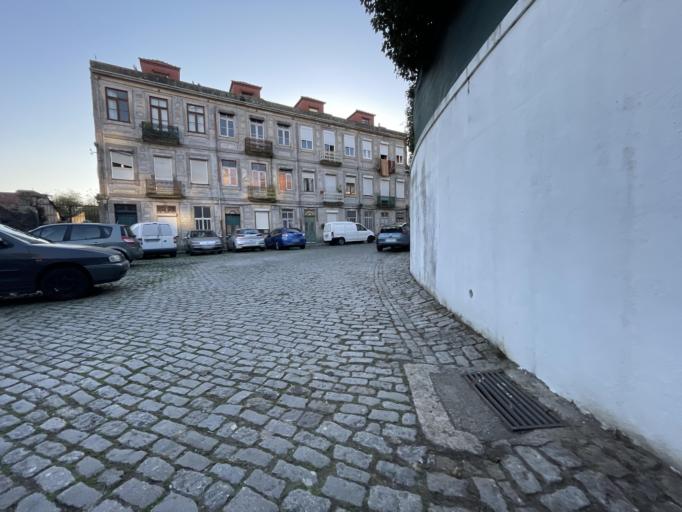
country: PT
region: Porto
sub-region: Porto
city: Porto
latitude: 41.1561
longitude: -8.5976
